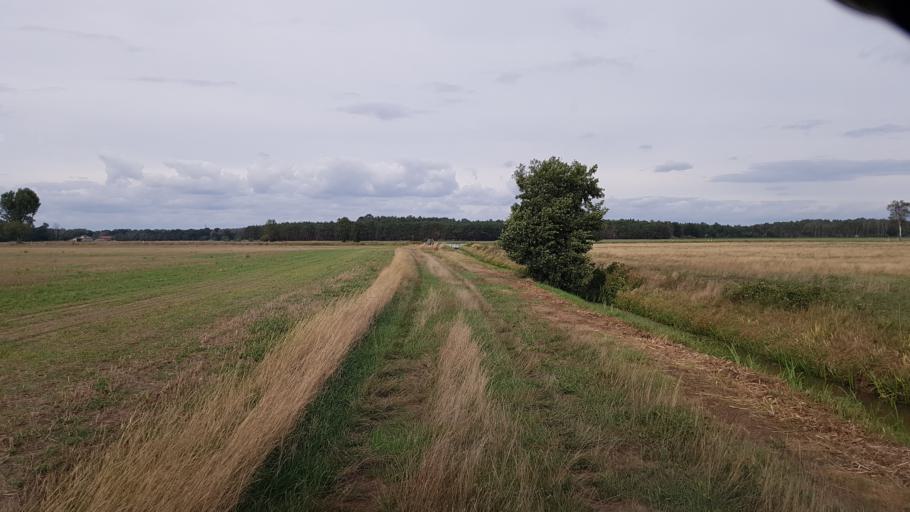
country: DE
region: Brandenburg
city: Schilda
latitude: 51.5556
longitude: 13.3493
